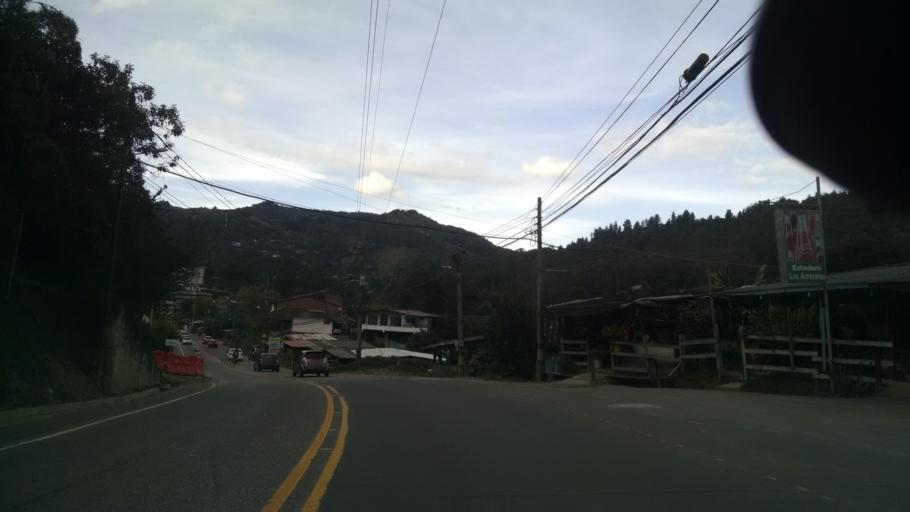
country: CO
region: Antioquia
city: El Retiro
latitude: 6.1137
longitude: -75.5007
